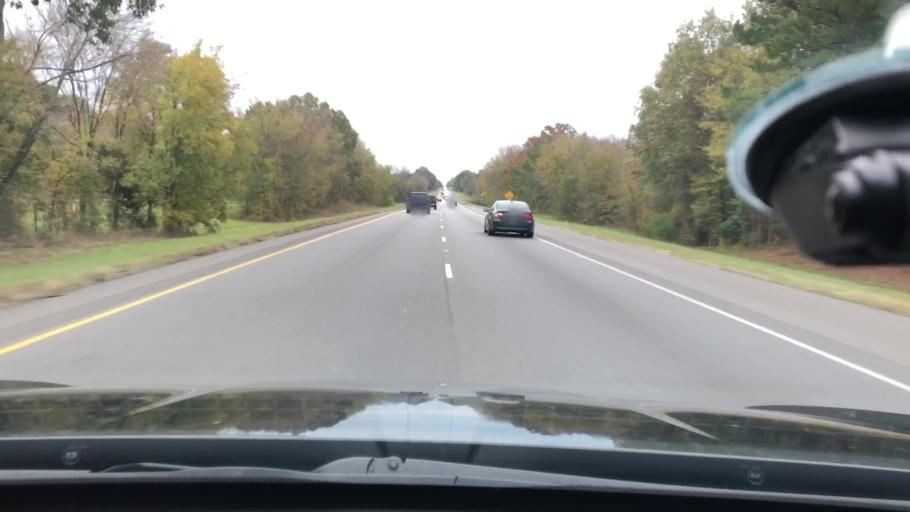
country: US
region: Arkansas
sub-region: Hempstead County
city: Hope
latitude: 33.6385
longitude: -93.7026
